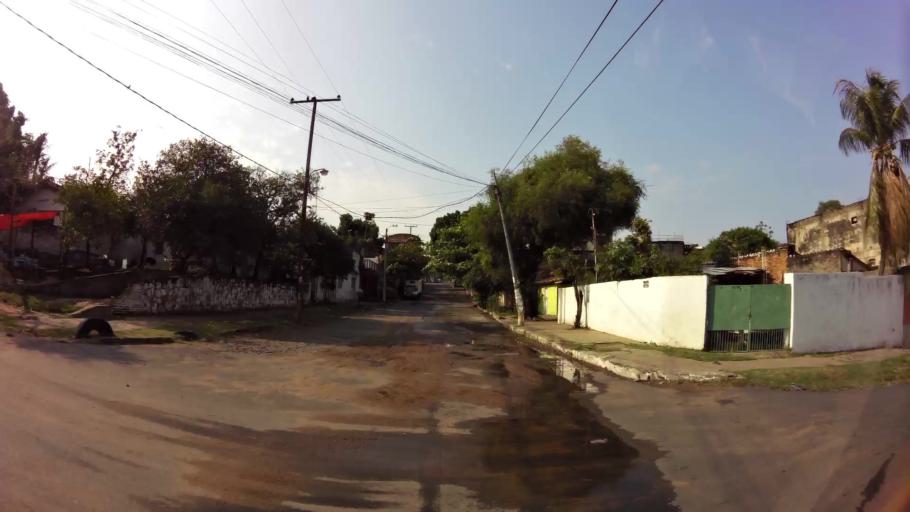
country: PY
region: Presidente Hayes
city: Nanawa
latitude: -25.2814
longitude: -57.6619
